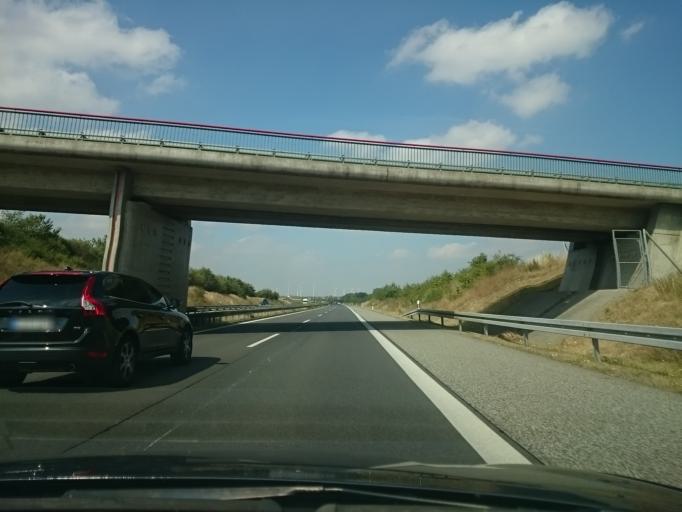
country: DE
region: Brandenburg
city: Grunow
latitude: 53.3296
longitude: 13.9872
